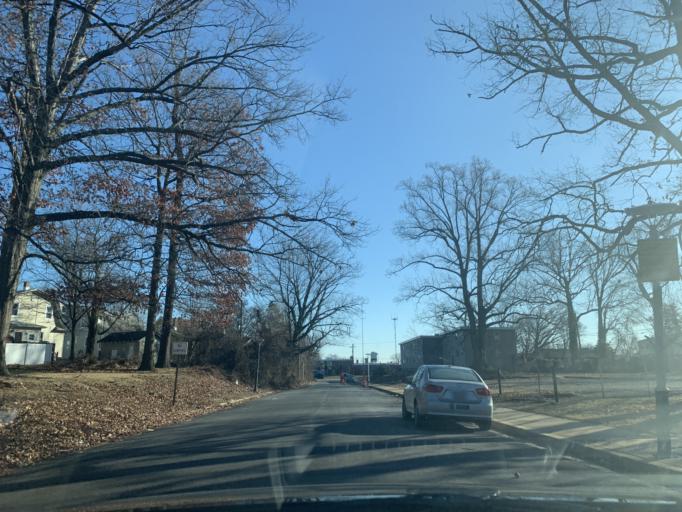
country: US
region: Maryland
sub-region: Baltimore County
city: Lochearn
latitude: 39.3360
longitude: -76.6809
